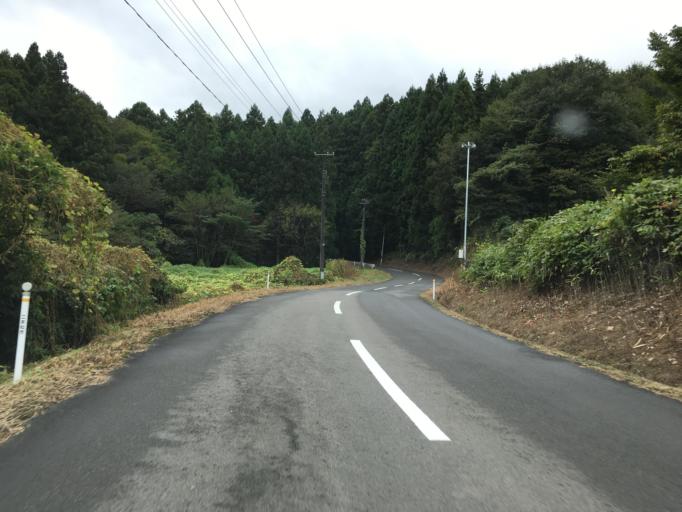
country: JP
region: Fukushima
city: Nihommatsu
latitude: 37.6306
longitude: 140.4376
